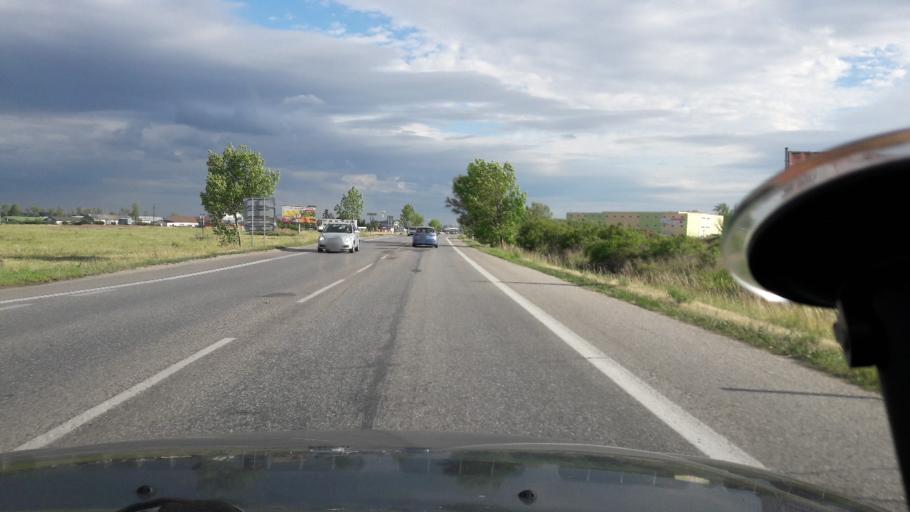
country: SK
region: Bratislavsky
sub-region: Okres Pezinok
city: Pezinok
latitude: 48.2974
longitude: 17.2812
